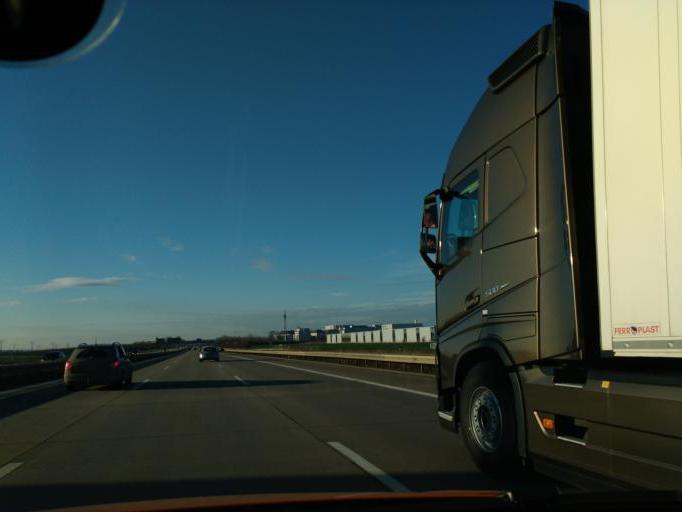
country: DE
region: Saxony-Anhalt
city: Barleben
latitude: 52.1851
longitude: 11.6128
